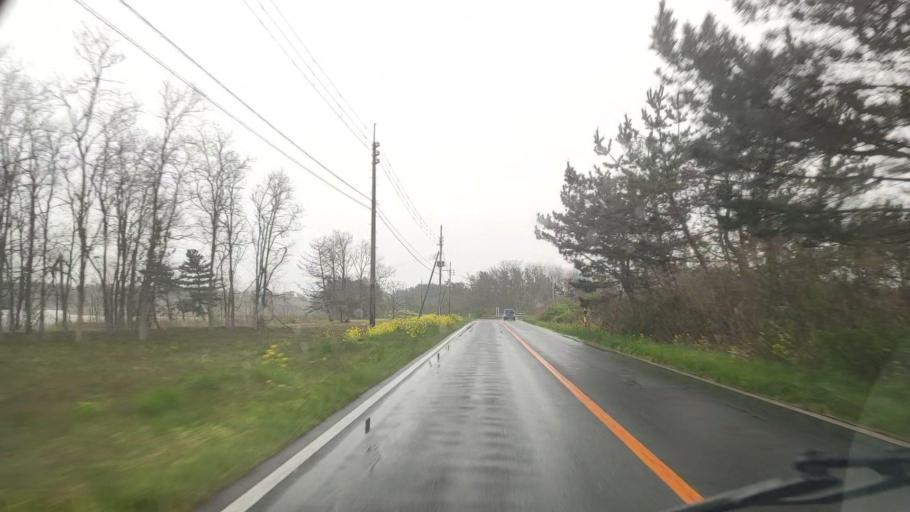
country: JP
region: Akita
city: Tenno
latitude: 40.0374
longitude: 139.9540
